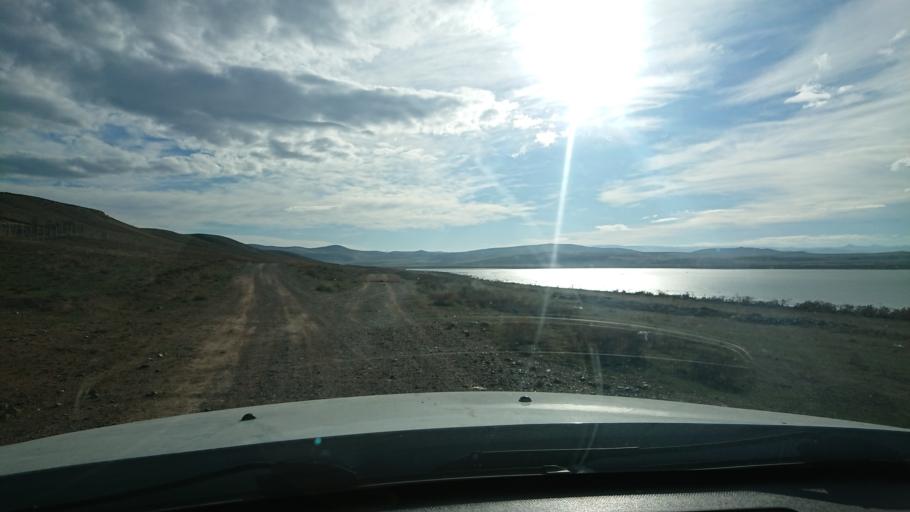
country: TR
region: Aksaray
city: Sariyahsi
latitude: 39.0502
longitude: 33.9743
